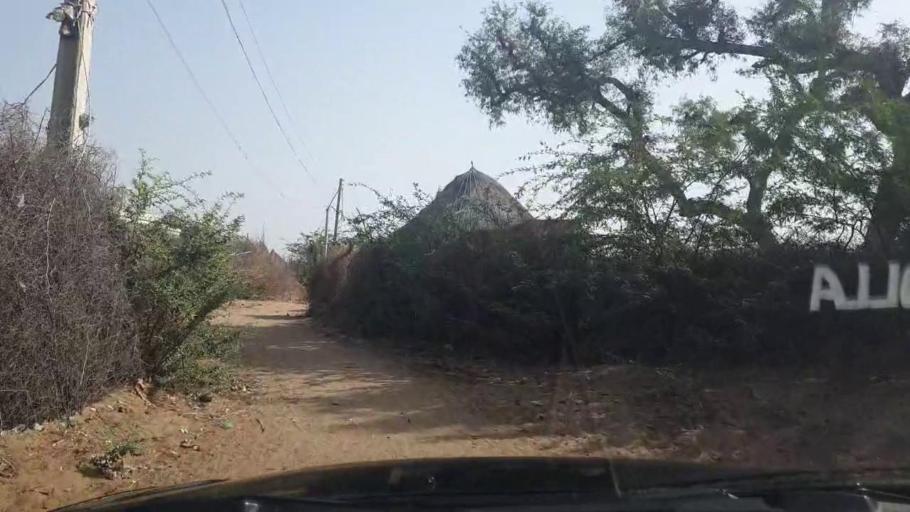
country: PK
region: Sindh
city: Islamkot
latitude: 25.0087
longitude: 70.2102
